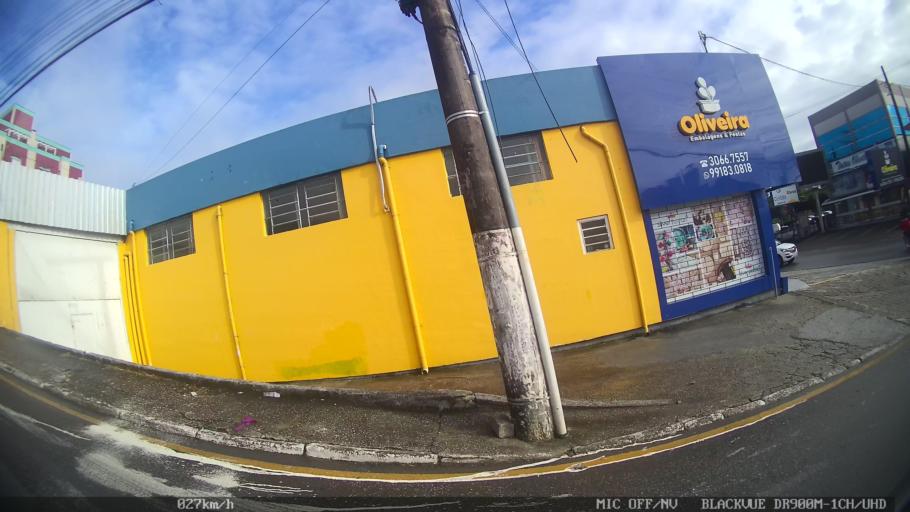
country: BR
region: Santa Catarina
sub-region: Sao Jose
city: Campinas
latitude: -27.6067
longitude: -48.6336
